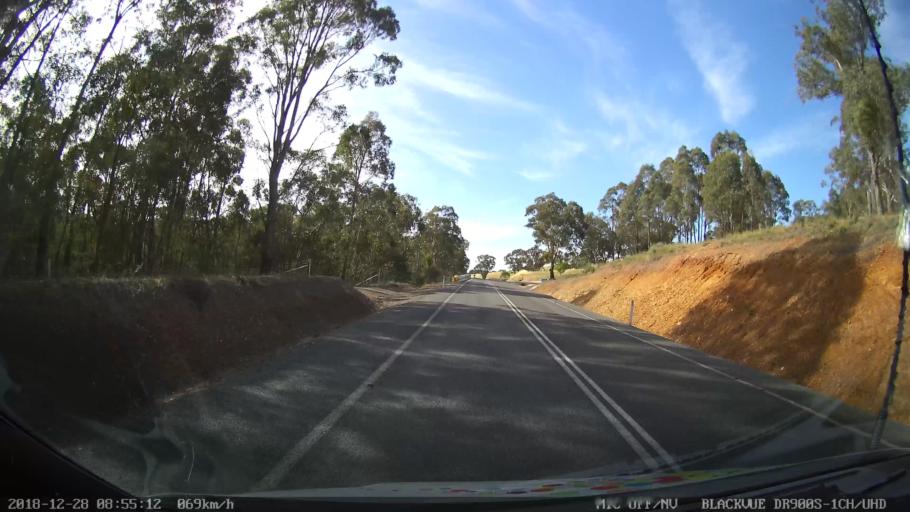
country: AU
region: New South Wales
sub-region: Upper Lachlan Shire
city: Crookwell
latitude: -34.0986
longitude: 149.3318
